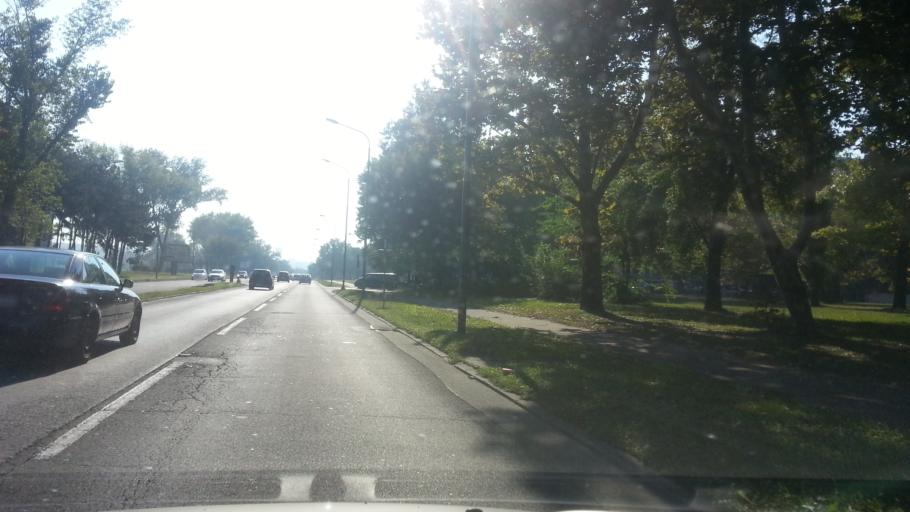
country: RS
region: Central Serbia
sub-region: Belgrade
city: Novi Beograd
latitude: 44.8228
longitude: 20.4257
